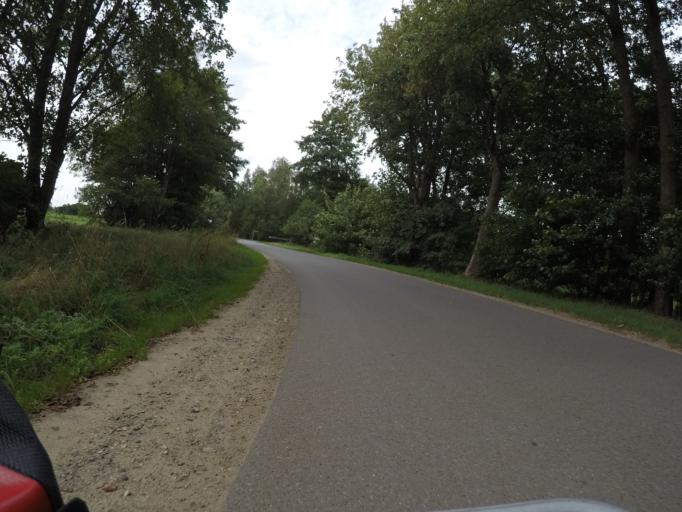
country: DE
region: Lower Saxony
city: Bardowick
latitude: 53.3050
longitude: 10.4040
